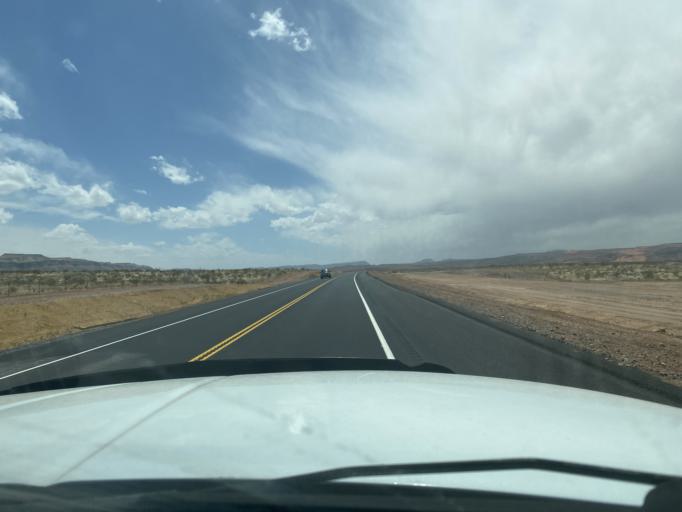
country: US
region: Utah
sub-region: Washington County
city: Hurricane
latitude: 37.1510
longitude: -113.3458
